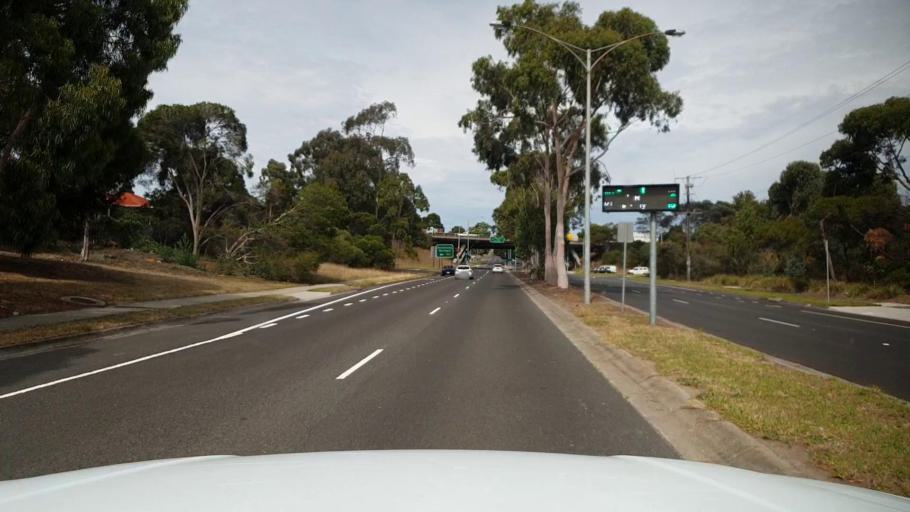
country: AU
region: Victoria
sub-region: Monash
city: Notting Hill
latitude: -37.8909
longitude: 145.1309
